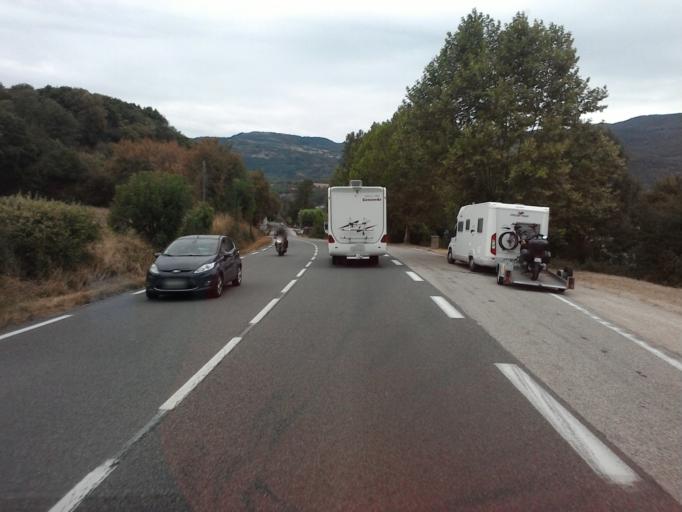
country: FR
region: Rhone-Alpes
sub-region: Departement de l'Ain
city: Sault-Brenaz
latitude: 45.8406
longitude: 5.4157
